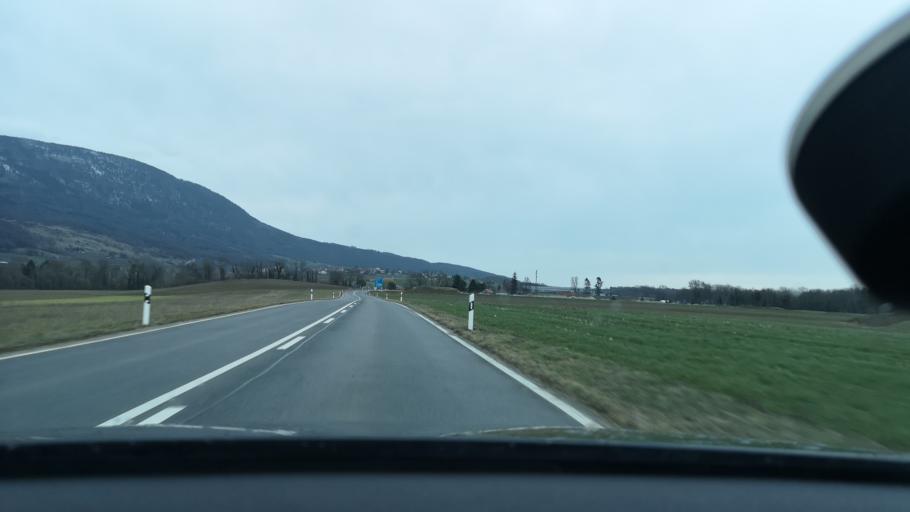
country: CH
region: Vaud
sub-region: Jura-Nord vaudois District
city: Grandson
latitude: 46.8249
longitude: 6.6697
